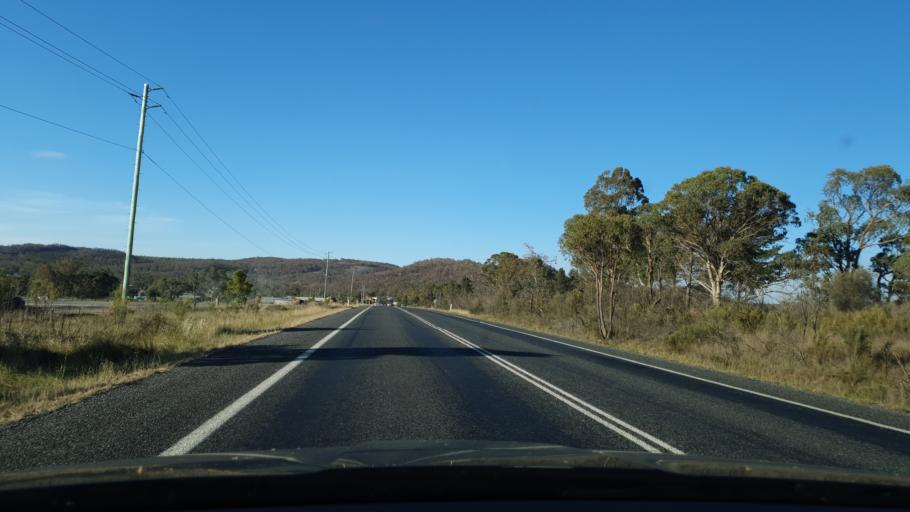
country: AU
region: Queensland
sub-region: Southern Downs
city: Stanthorpe
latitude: -28.6606
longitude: 151.9164
